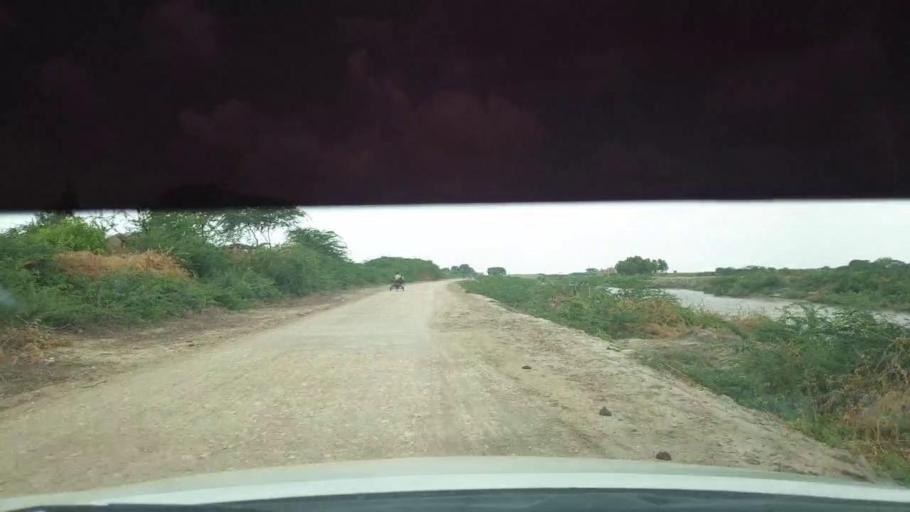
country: PK
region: Sindh
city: Kadhan
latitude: 24.4714
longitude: 69.0535
